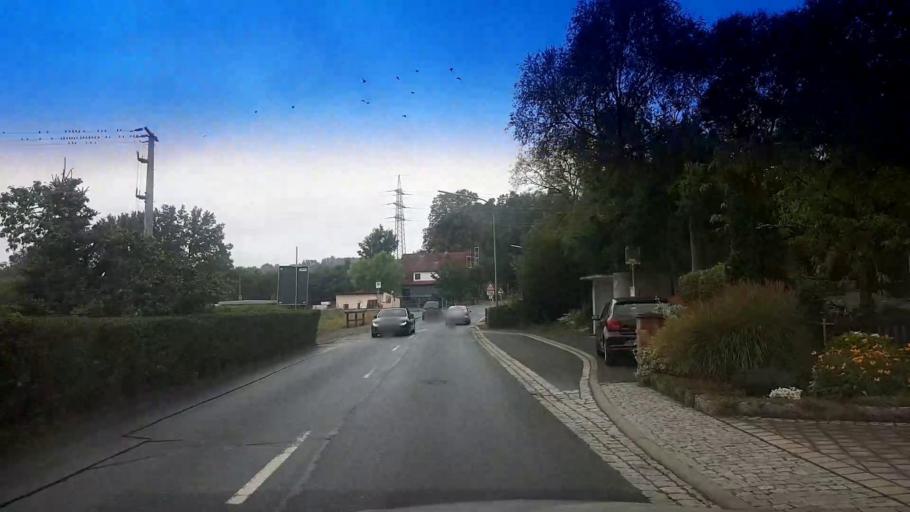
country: DE
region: Bavaria
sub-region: Upper Franconia
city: Heroldsbach
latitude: 49.7042
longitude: 11.0118
